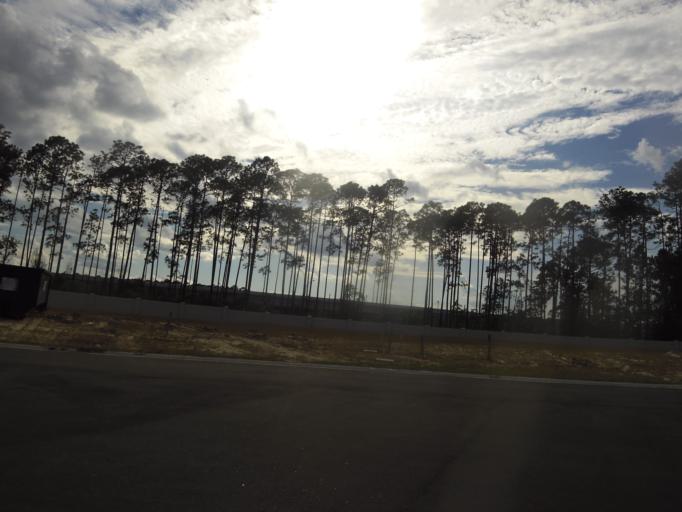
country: US
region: Florida
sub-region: Saint Johns County
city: Palm Valley
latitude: 30.1790
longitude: -81.5122
